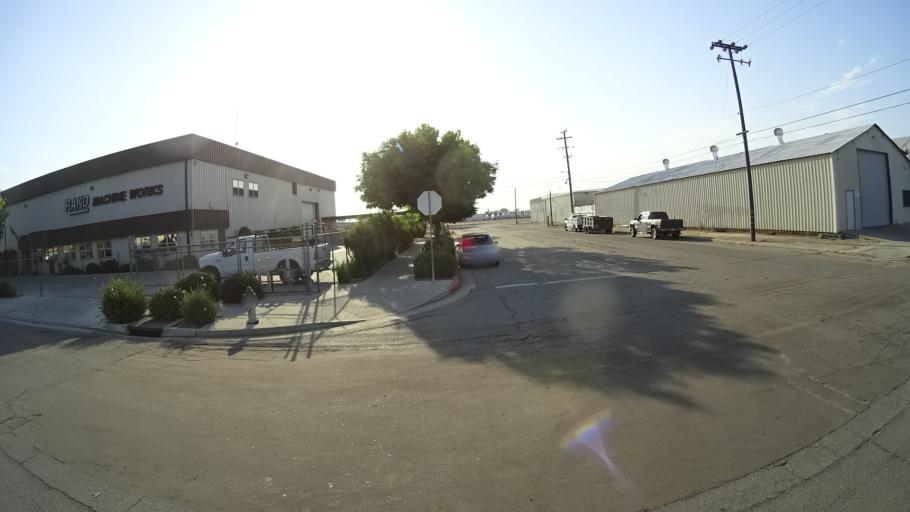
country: US
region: California
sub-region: Fresno County
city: Fresno
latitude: 36.7227
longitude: -119.7764
